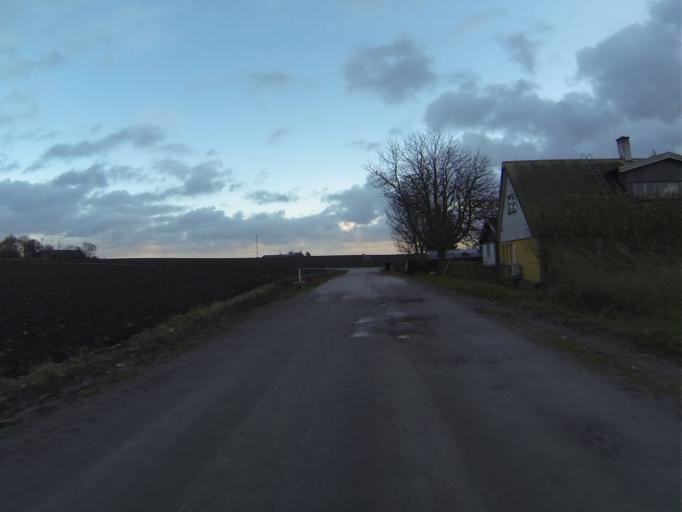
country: SE
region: Skane
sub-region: Lunds Kommun
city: Genarp
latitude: 55.6410
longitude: 13.3355
